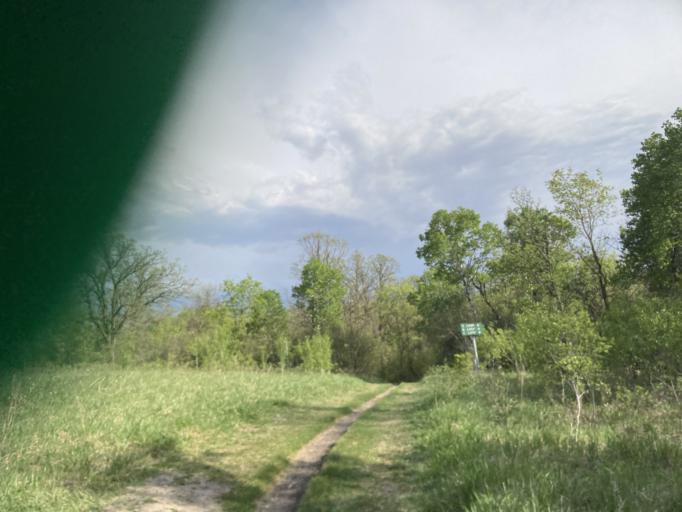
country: CA
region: Manitoba
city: Brandon
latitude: 49.7224
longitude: -99.9083
